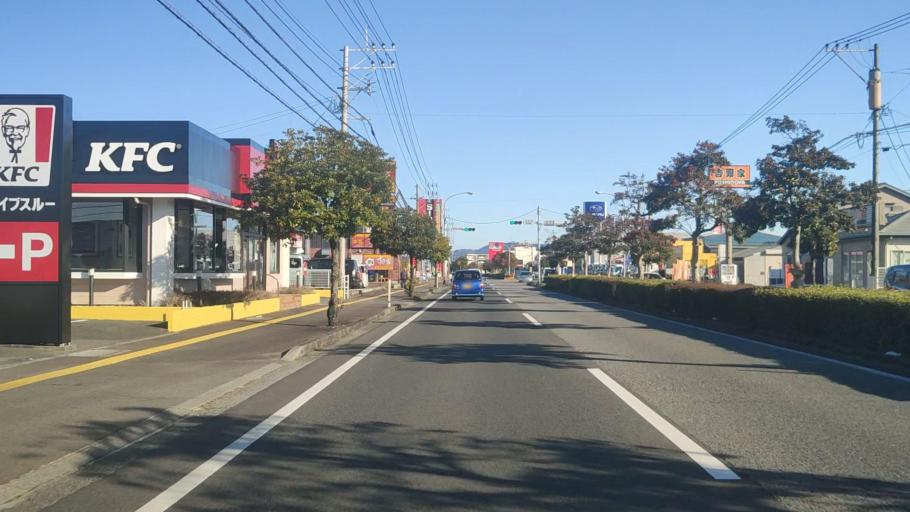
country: JP
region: Miyazaki
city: Nobeoka
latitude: 32.5655
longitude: 131.6825
